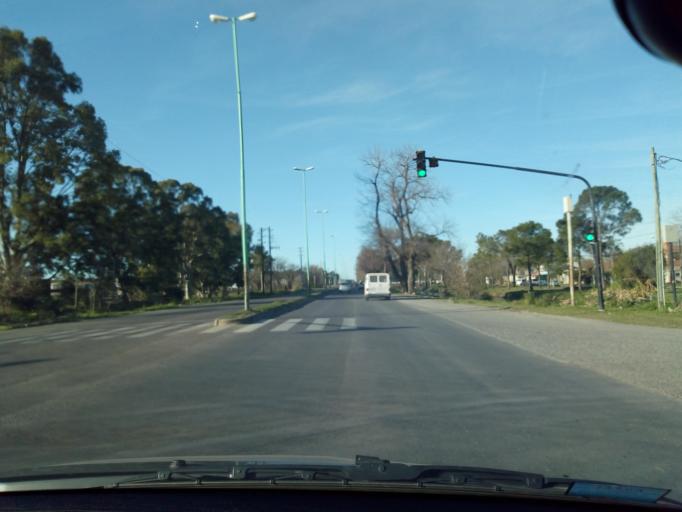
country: AR
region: Buenos Aires
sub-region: Partido de Ensenada
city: Ensenada
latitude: -34.8758
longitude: -57.9177
